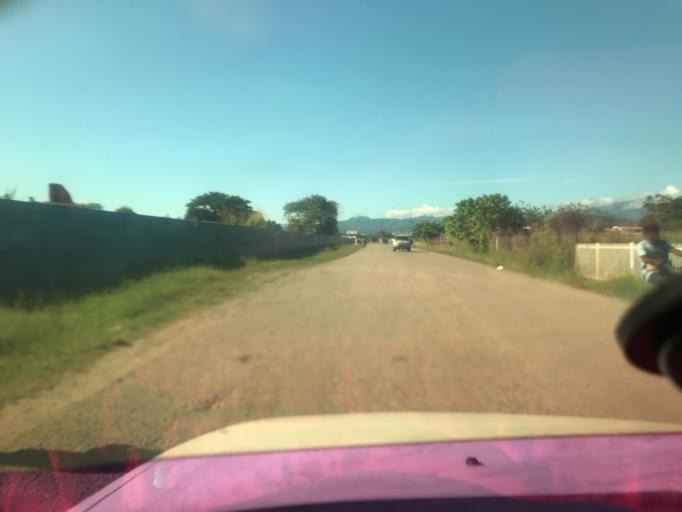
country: SB
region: Guadalcanal
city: Honiara
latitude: -9.4266
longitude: 160.0473
